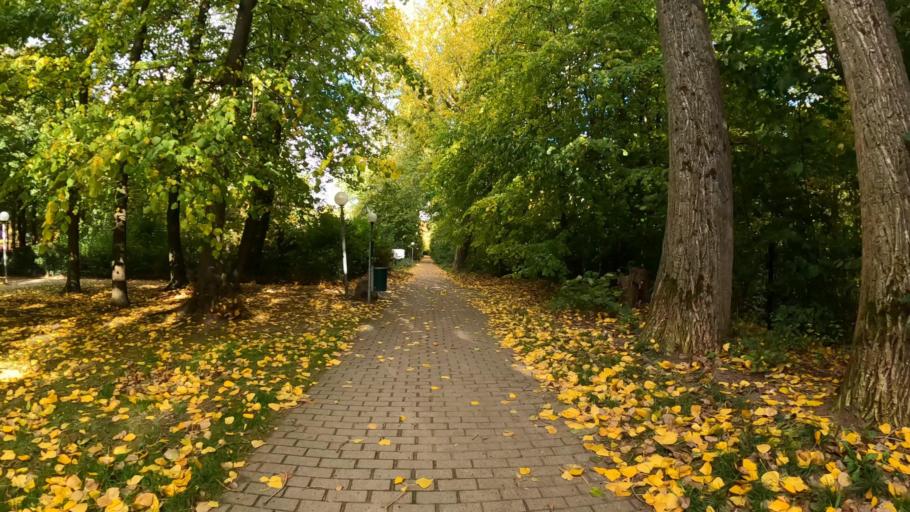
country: DE
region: Schleswig-Holstein
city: Delingsdorf
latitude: 53.6855
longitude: 10.2460
